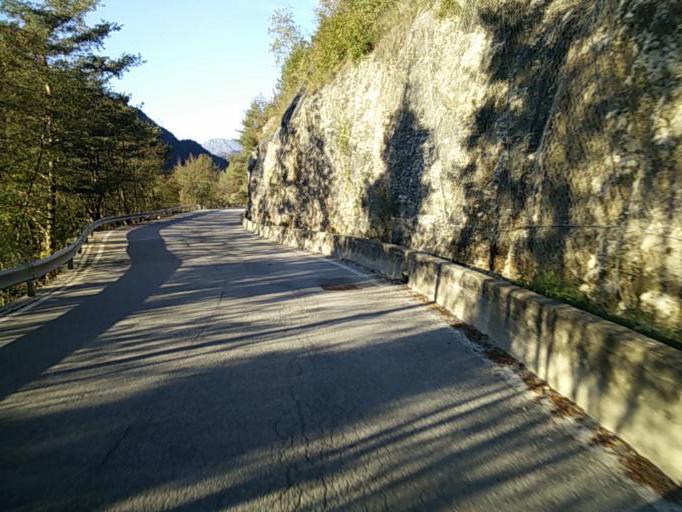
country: IT
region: Lombardy
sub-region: Provincia di Brescia
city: Gargnano
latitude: 45.6912
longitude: 10.6109
